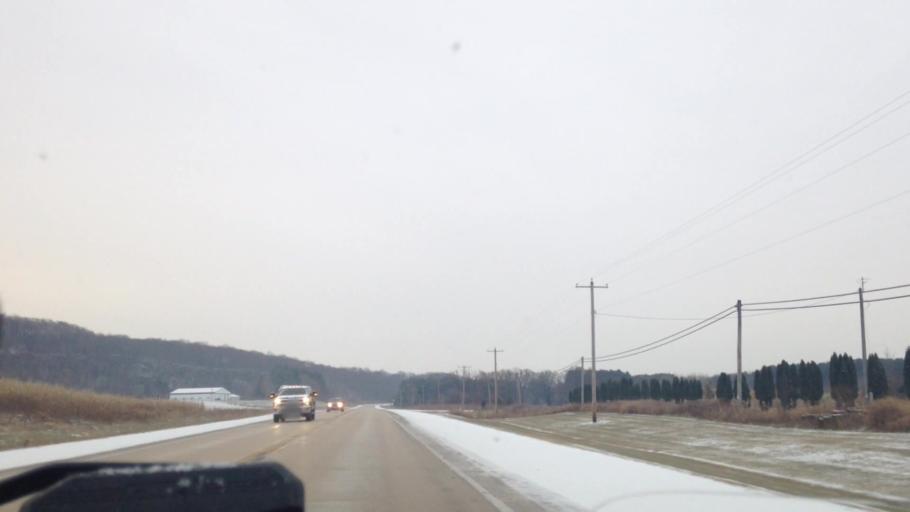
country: US
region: Wisconsin
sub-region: Dodge County
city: Mayville
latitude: 43.4628
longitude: -88.5454
